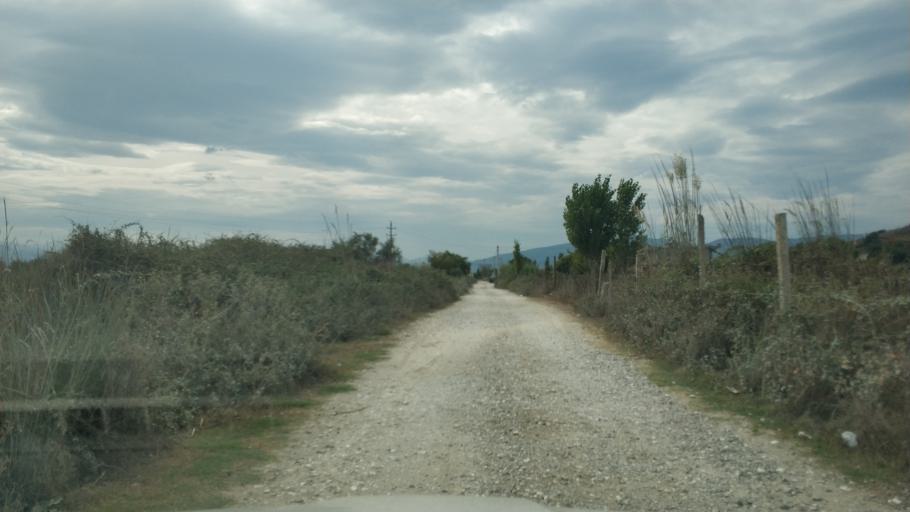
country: AL
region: Vlore
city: Vlore
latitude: 40.5051
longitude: 19.4094
